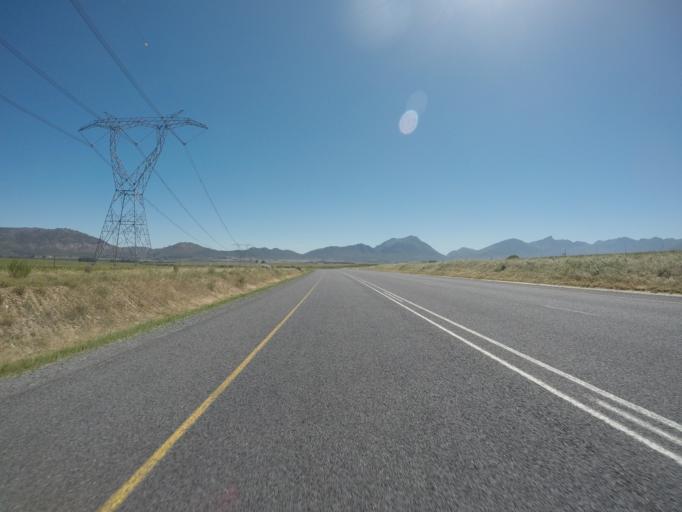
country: ZA
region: Western Cape
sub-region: Cape Winelands District Municipality
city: Ceres
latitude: -33.3282
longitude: 19.1547
